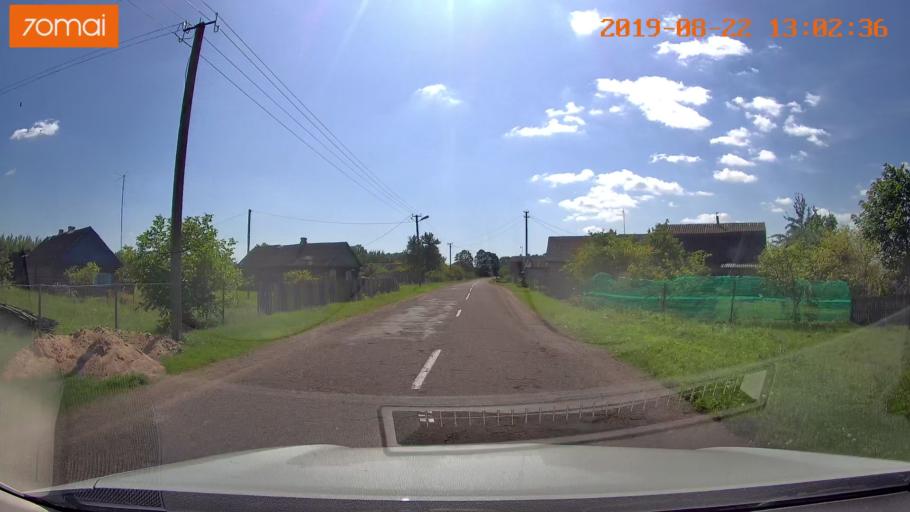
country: BY
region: Minsk
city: Prawdzinski
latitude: 53.3874
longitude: 27.8253
